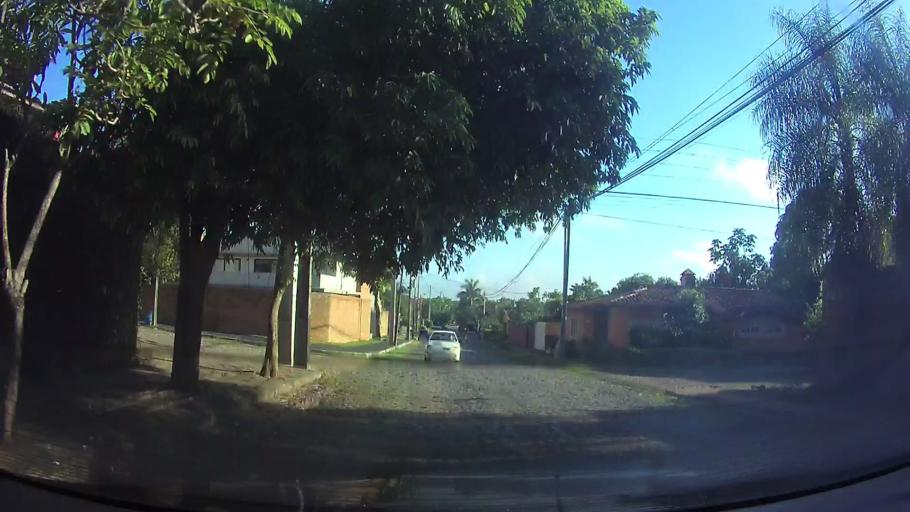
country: PY
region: Central
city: Fernando de la Mora
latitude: -25.2665
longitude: -57.5506
